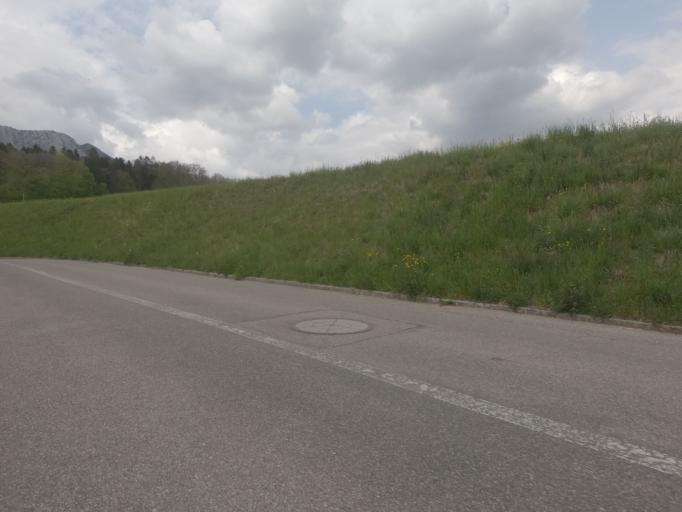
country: CH
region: Solothurn
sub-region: Bezirk Lebern
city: Riedholz
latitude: 47.2346
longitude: 7.5612
